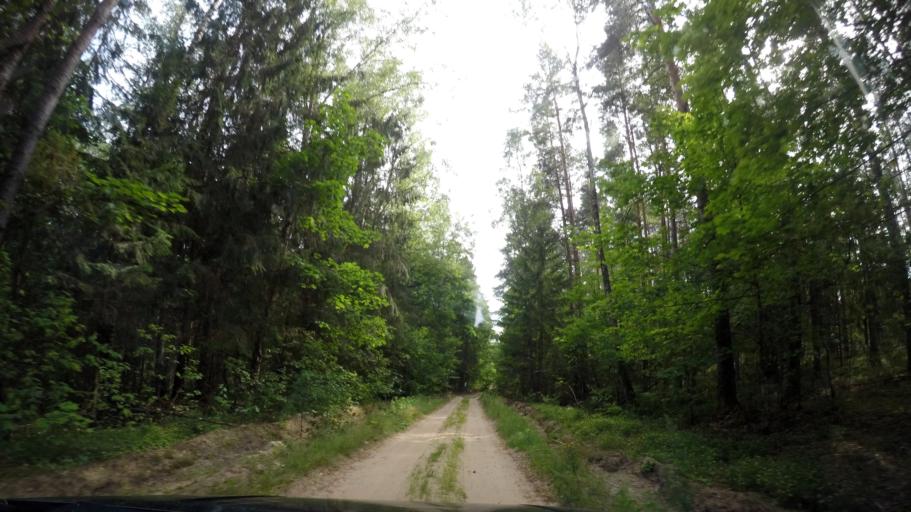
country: BY
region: Grodnenskaya
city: Skidal'
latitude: 53.8274
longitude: 24.1795
